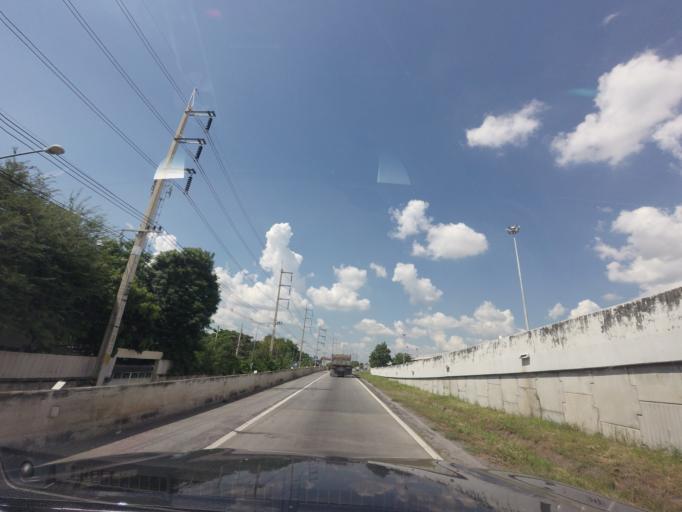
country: TH
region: Nakhon Ratchasima
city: Nakhon Ratchasima
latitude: 14.9609
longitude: 102.0529
